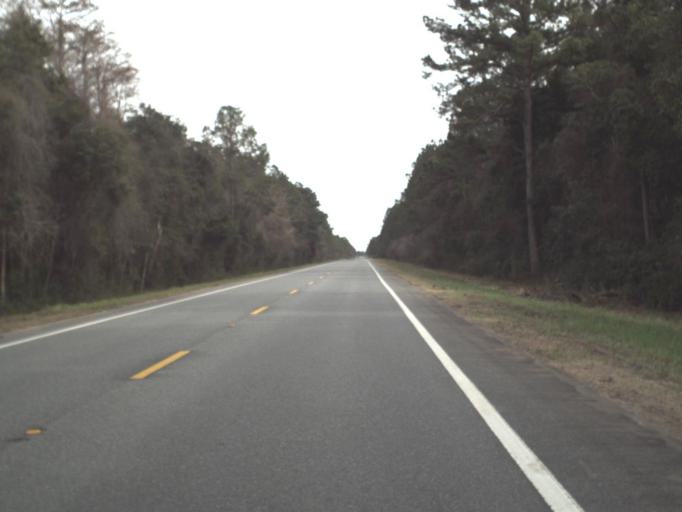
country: US
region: Florida
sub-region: Wakulla County
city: Crawfordville
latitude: 30.3130
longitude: -84.4385
